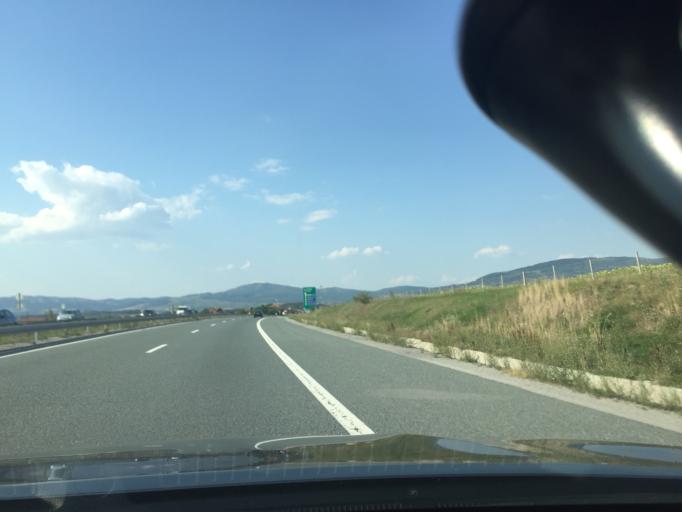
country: BG
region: Pernik
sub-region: Obshtina Pernik
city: Pernik
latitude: 42.5894
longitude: 23.1199
